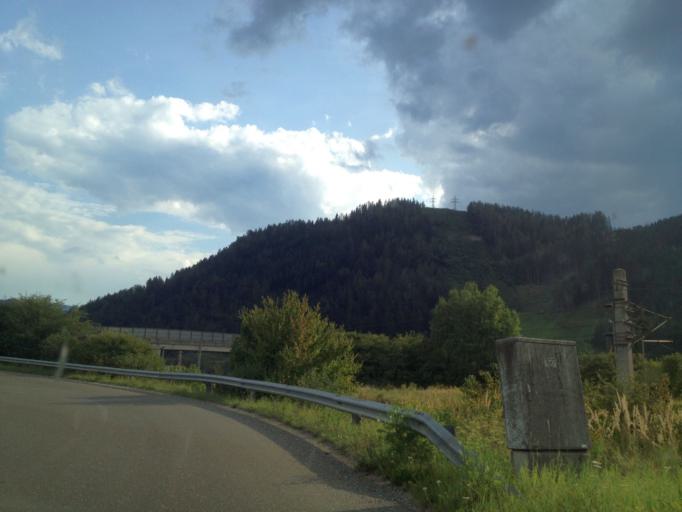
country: AT
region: Styria
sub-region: Politischer Bezirk Leoben
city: Sankt Michael in Obersteiermark
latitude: 47.3563
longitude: 15.0051
